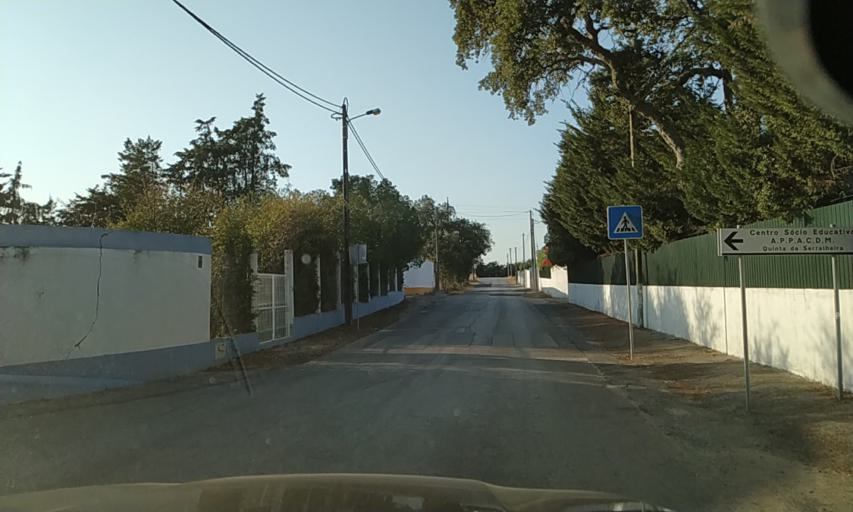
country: PT
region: Setubal
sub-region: Setubal
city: Setubal
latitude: 38.5469
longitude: -8.8409
